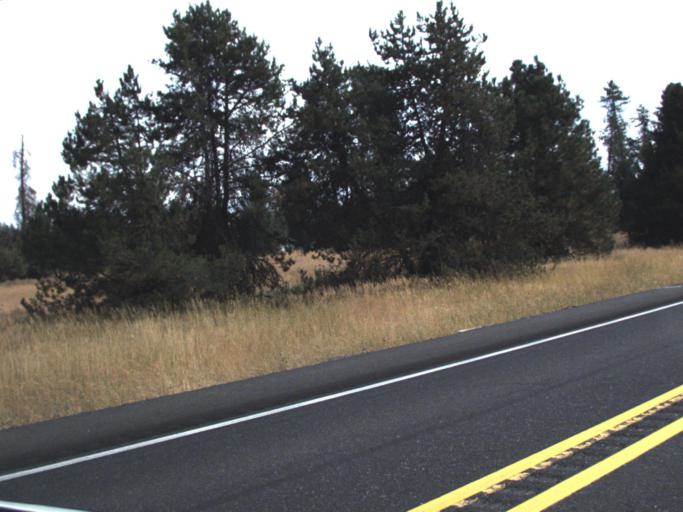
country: US
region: Washington
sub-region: Spokane County
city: Deer Park
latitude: 47.9520
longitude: -117.4863
